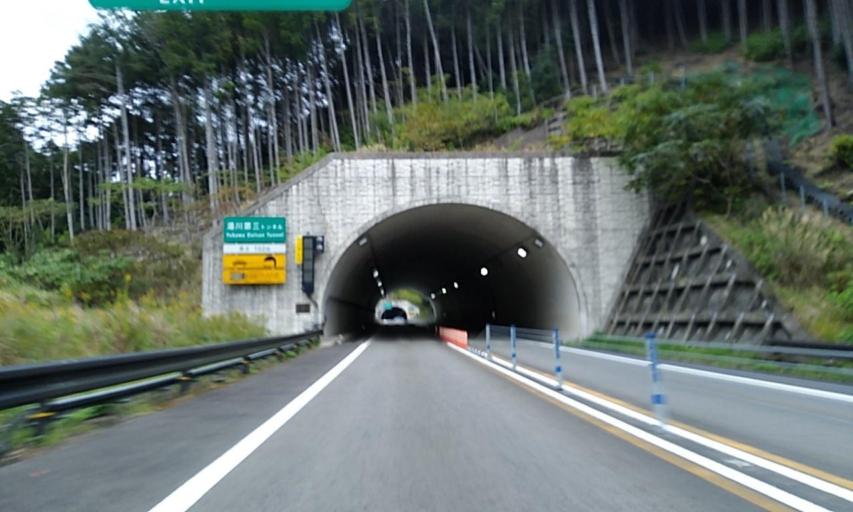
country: JP
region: Wakayama
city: Shingu
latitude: 33.6332
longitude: 135.9242
